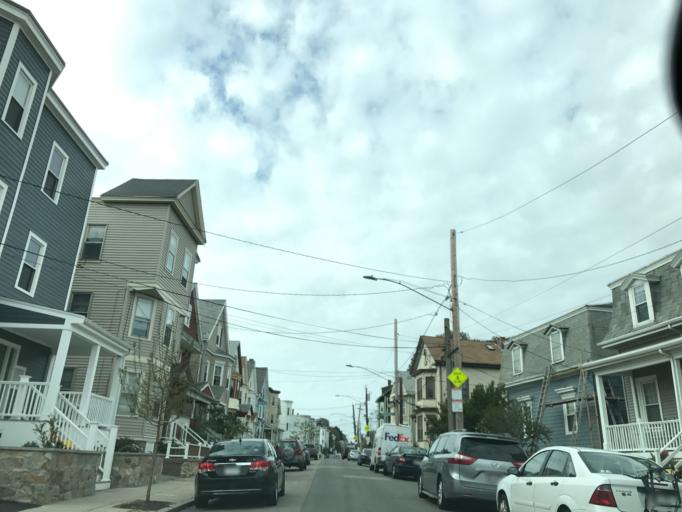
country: US
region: Massachusetts
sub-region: Suffolk County
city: South Boston
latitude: 42.3170
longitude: -71.0528
